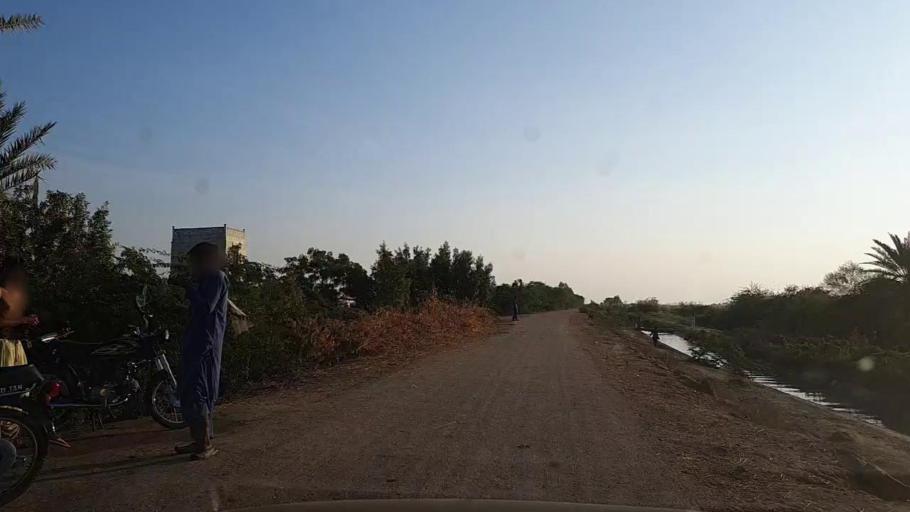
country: PK
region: Sindh
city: Thatta
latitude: 24.6212
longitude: 67.9136
